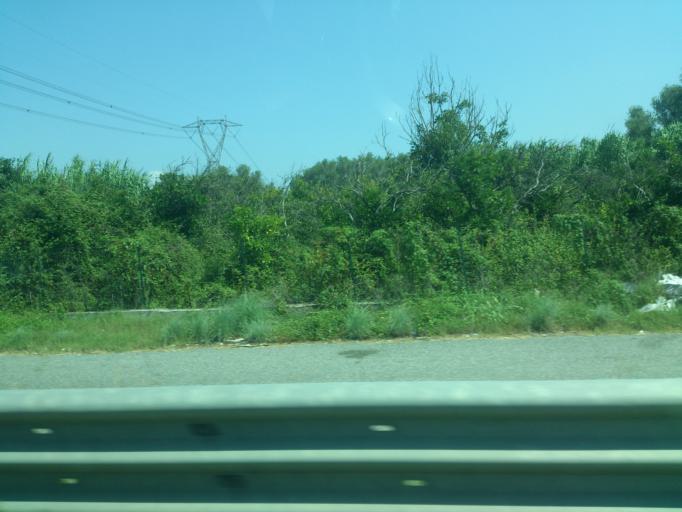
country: IT
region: Calabria
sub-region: Provincia di Reggio Calabria
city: Rosarno
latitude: 38.4674
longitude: 16.0087
